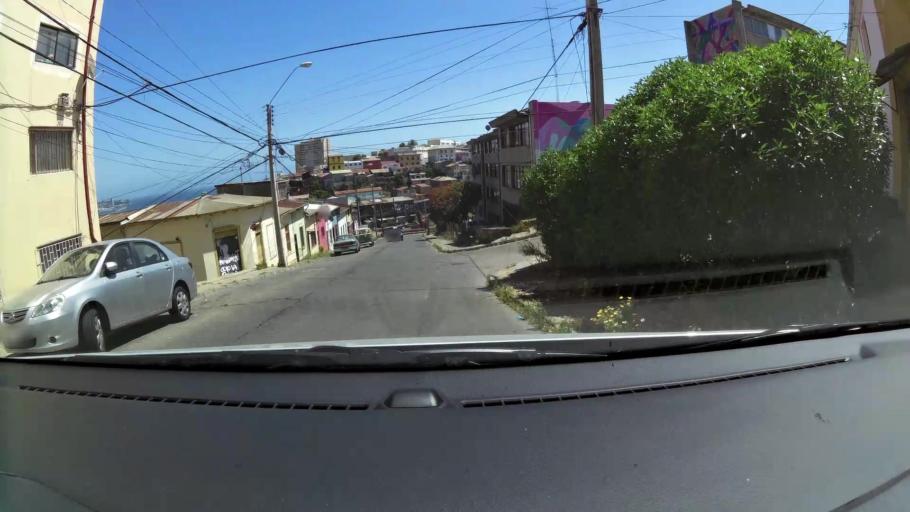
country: CL
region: Valparaiso
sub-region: Provincia de Valparaiso
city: Valparaiso
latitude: -33.0463
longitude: -71.6008
